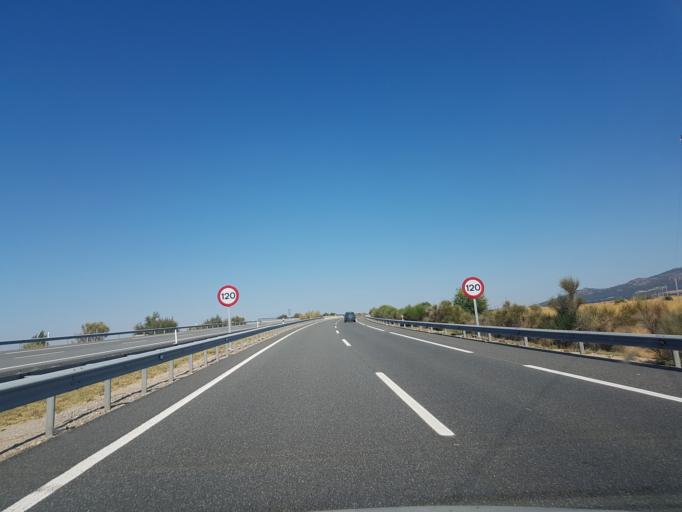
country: ES
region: Castille and Leon
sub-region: Provincia de Avila
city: Berrocalejo de Aragona
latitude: 40.6954
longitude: -4.5823
